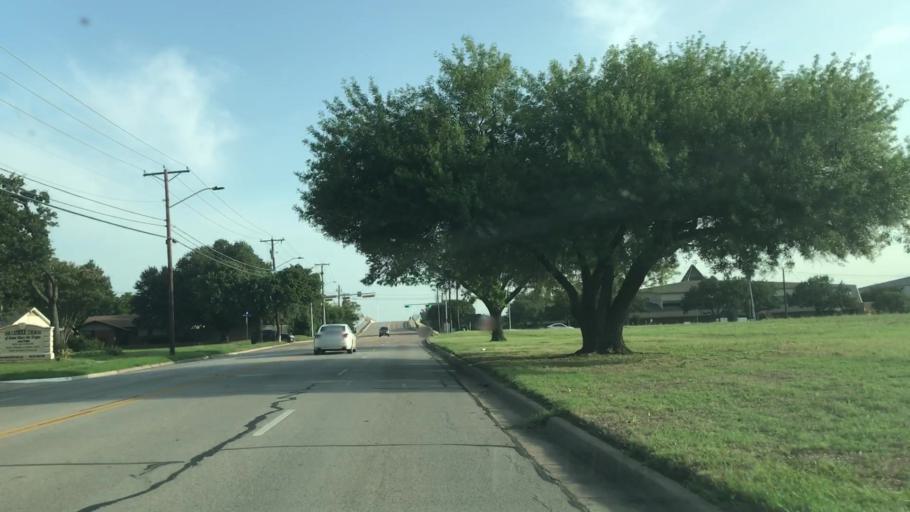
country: US
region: Texas
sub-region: Tarrant County
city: Arlington
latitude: 32.7563
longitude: -97.1231
